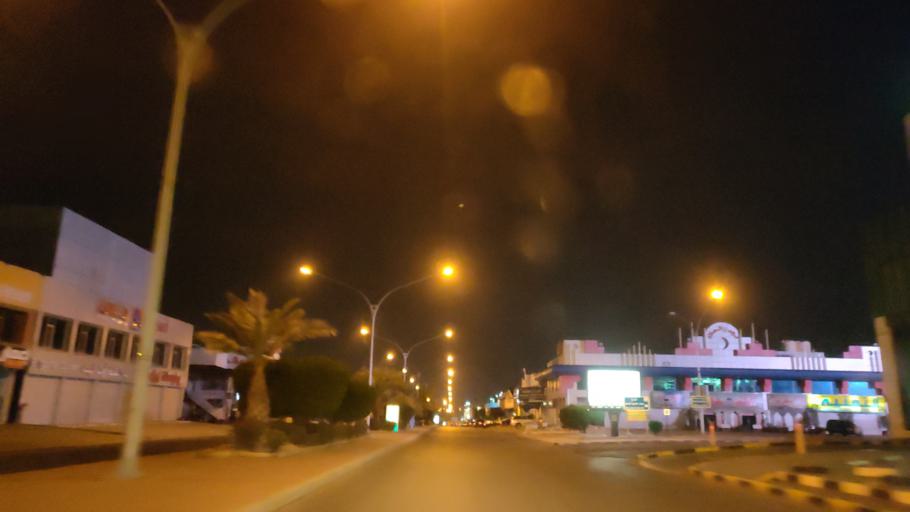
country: KW
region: Al Asimah
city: Ar Rabiyah
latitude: 29.3068
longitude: 47.9359
